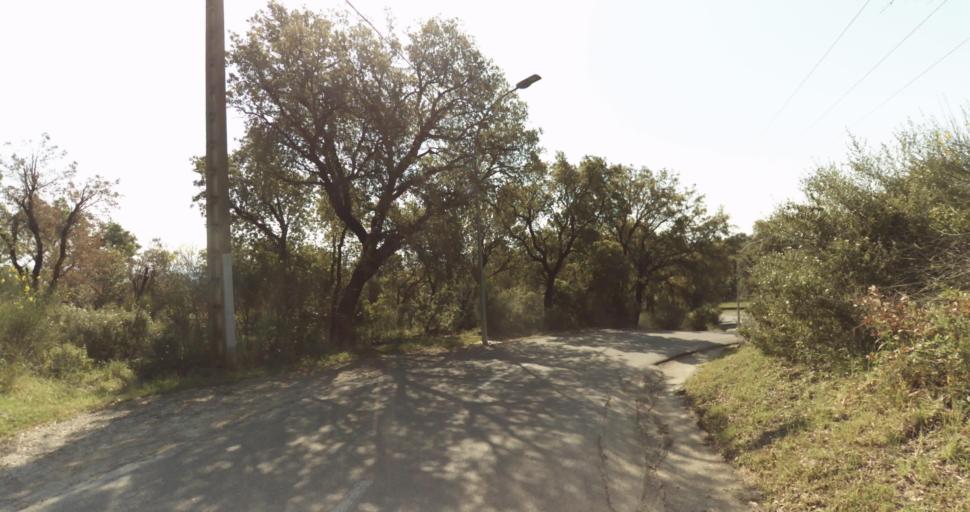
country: FR
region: Corsica
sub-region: Departement de la Haute-Corse
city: Biguglia
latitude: 42.6223
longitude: 9.4219
